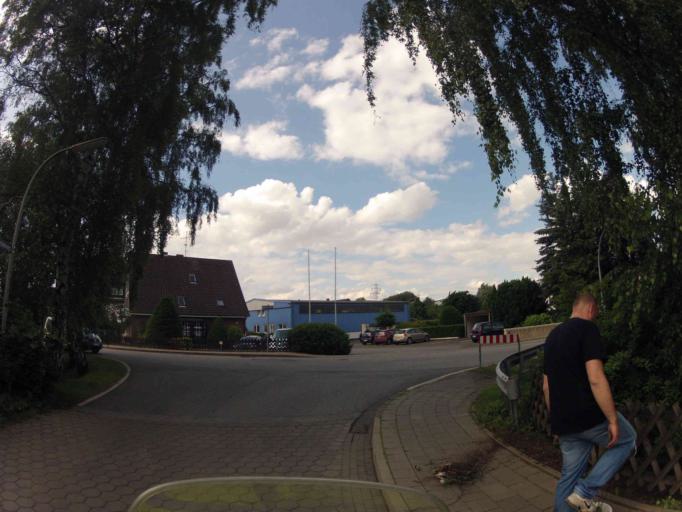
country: DE
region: Hamburg
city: Rothenburgsort
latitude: 53.5130
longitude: 10.0814
